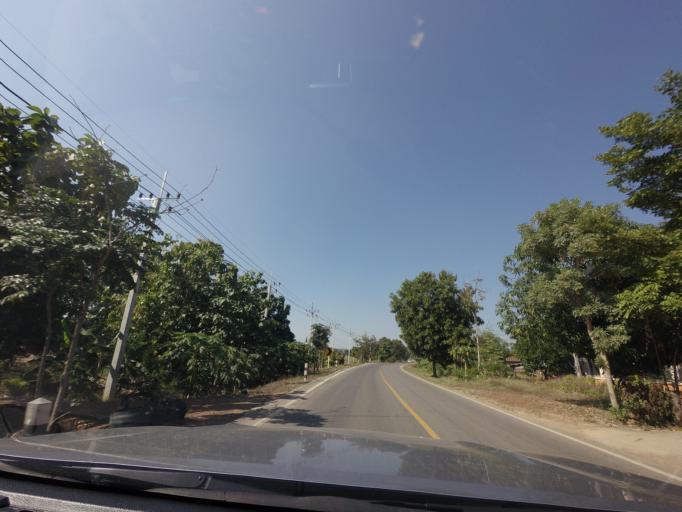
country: TH
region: Sukhothai
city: Sawankhalok
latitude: 17.3488
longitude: 99.8229
